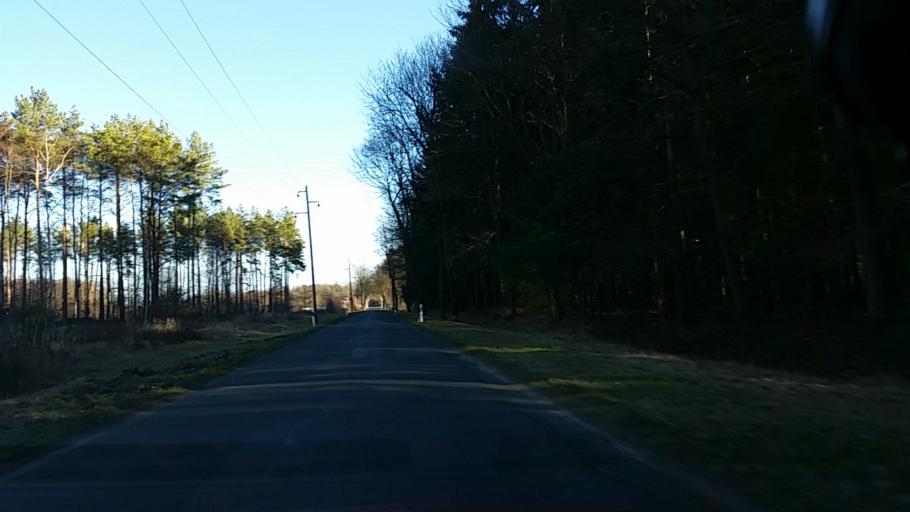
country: DE
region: Lower Saxony
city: Parsau
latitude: 52.5215
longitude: 10.9493
